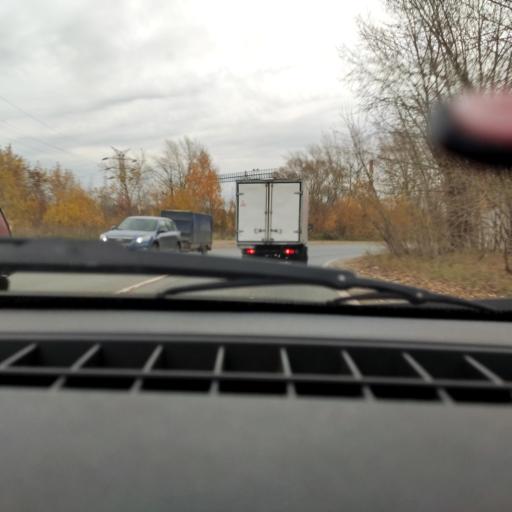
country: RU
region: Bashkortostan
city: Ufa
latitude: 54.8568
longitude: 56.0951
